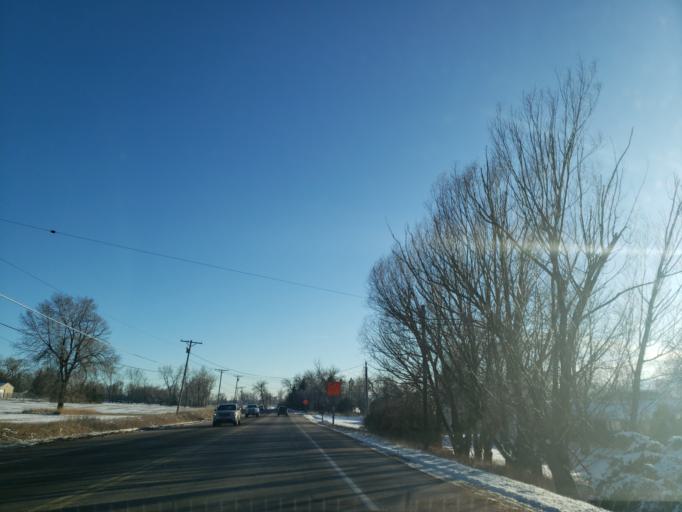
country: US
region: Colorado
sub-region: Larimer County
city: Fort Collins
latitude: 40.6230
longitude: -105.0719
